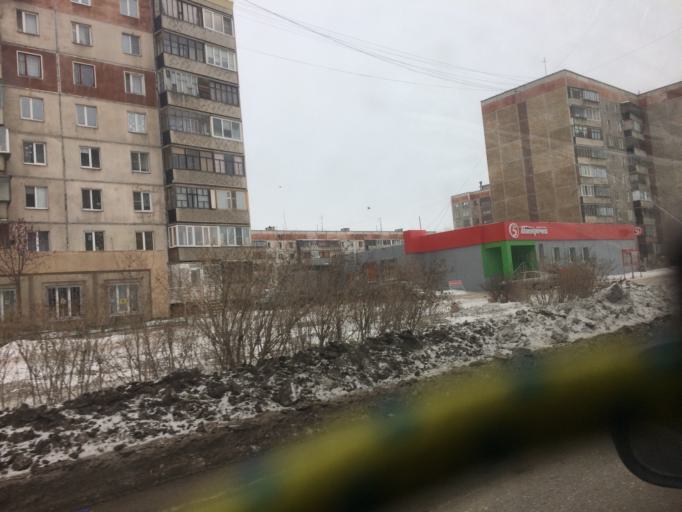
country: RU
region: Chelyabinsk
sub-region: Gorod Magnitogorsk
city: Magnitogorsk
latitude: 53.3610
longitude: 58.9823
